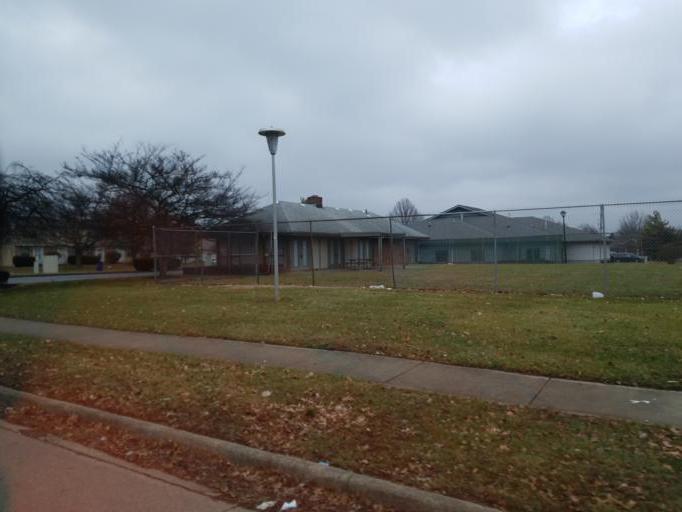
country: US
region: Ohio
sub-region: Franklin County
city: Minerva Park
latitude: 40.0931
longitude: -82.9522
